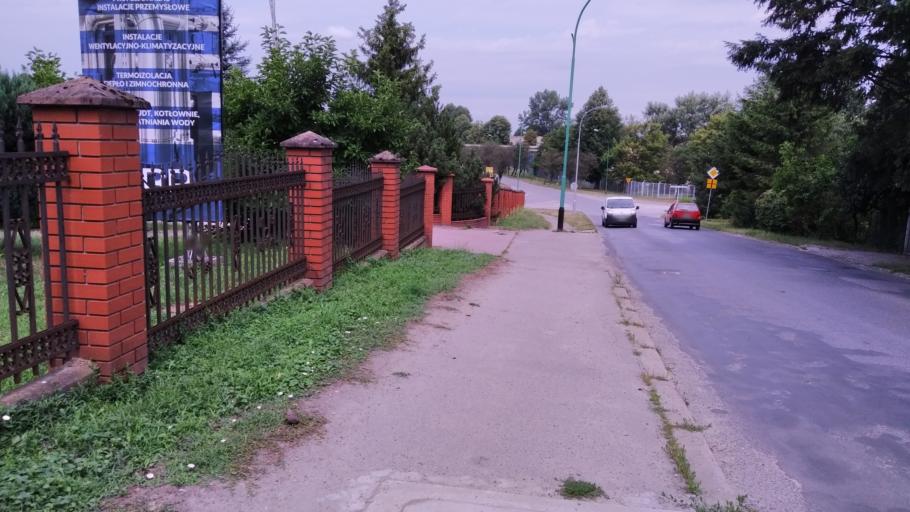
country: PL
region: Subcarpathian Voivodeship
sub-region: Powiat lancucki
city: Lancut
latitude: 50.0778
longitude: 22.2276
